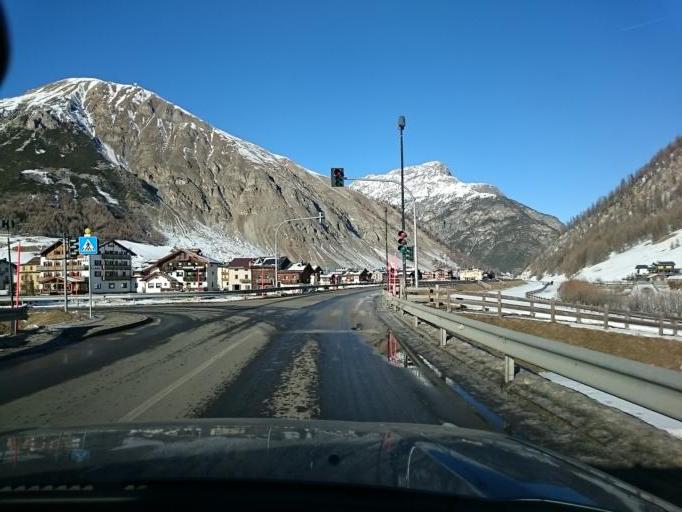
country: IT
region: Lombardy
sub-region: Provincia di Sondrio
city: Livigno
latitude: 46.5475
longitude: 10.1424
